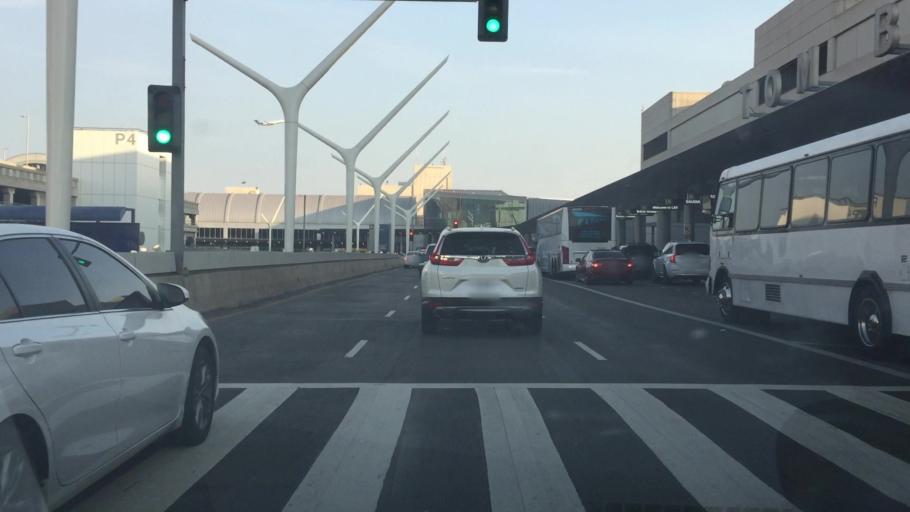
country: US
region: California
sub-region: Los Angeles County
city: El Segundo
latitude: 33.9440
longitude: -118.4082
